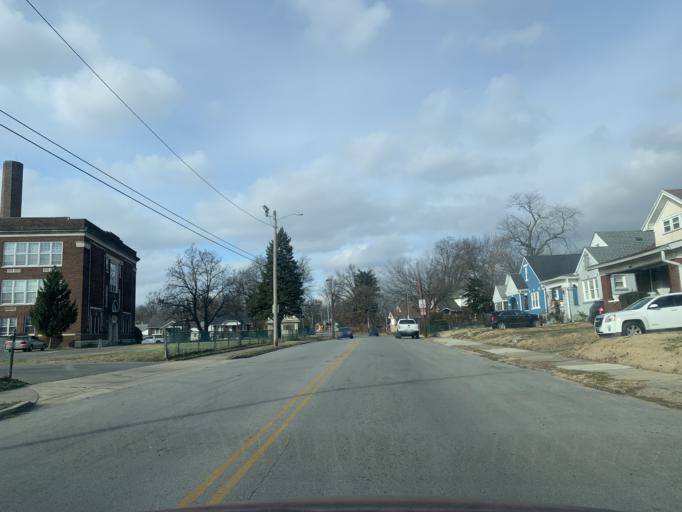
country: US
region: Kentucky
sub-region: Jefferson County
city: Shively
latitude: 38.2301
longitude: -85.7974
